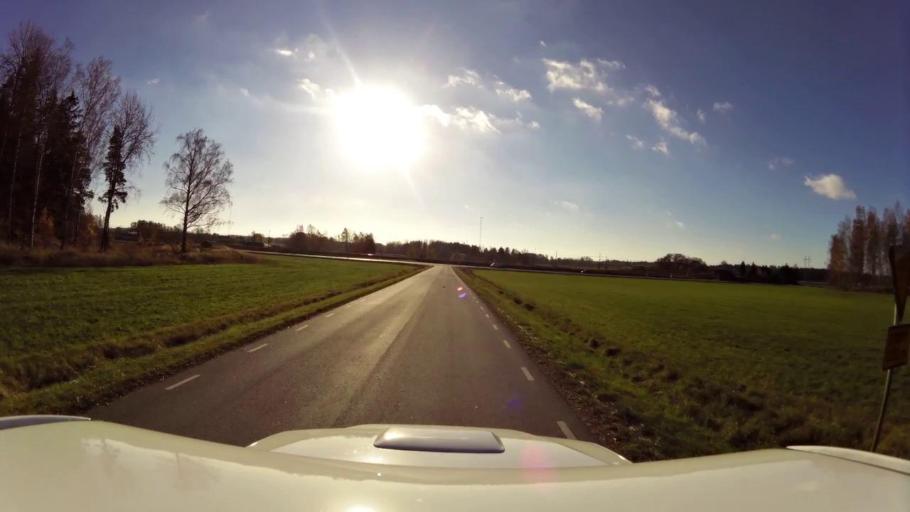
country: SE
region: OEstergoetland
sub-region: Linkopings Kommun
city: Linghem
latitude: 58.4379
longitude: 15.7769
